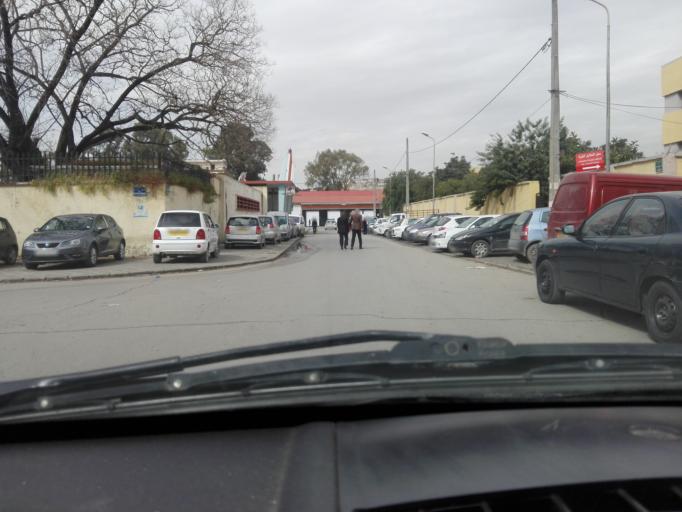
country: DZ
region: Alger
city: Bab Ezzouar
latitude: 36.7237
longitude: 3.1367
